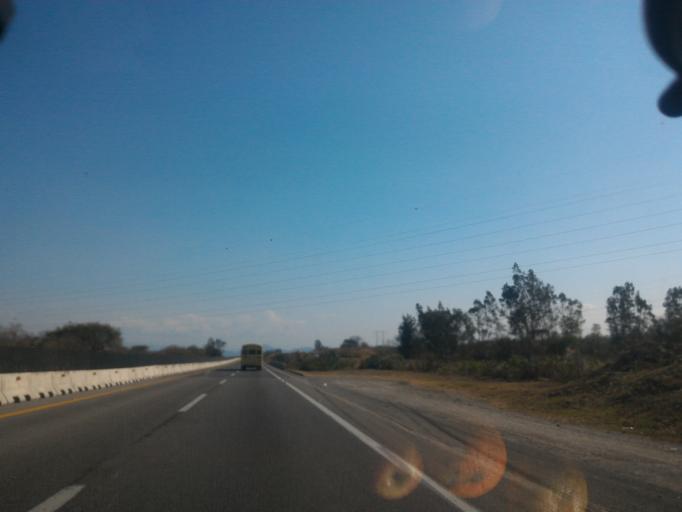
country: MX
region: Jalisco
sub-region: Zapotlan el Grande
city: Ciudad Guzman [CERESO]
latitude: 19.6394
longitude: -103.4690
